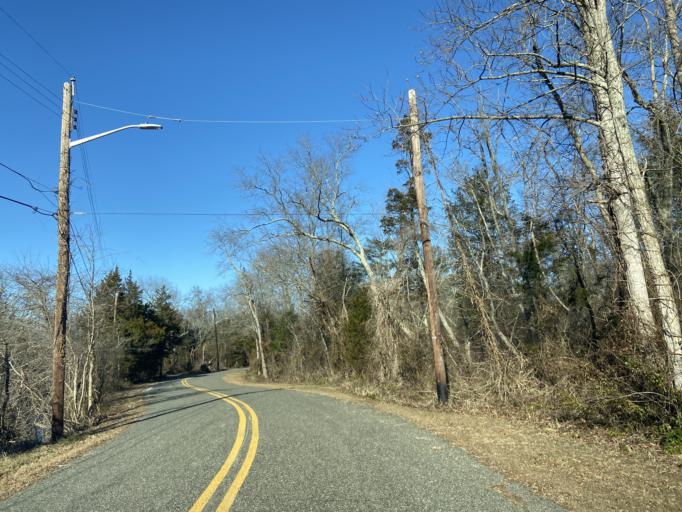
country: US
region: New Jersey
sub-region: Cumberland County
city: Vineland
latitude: 39.4935
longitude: -75.0742
